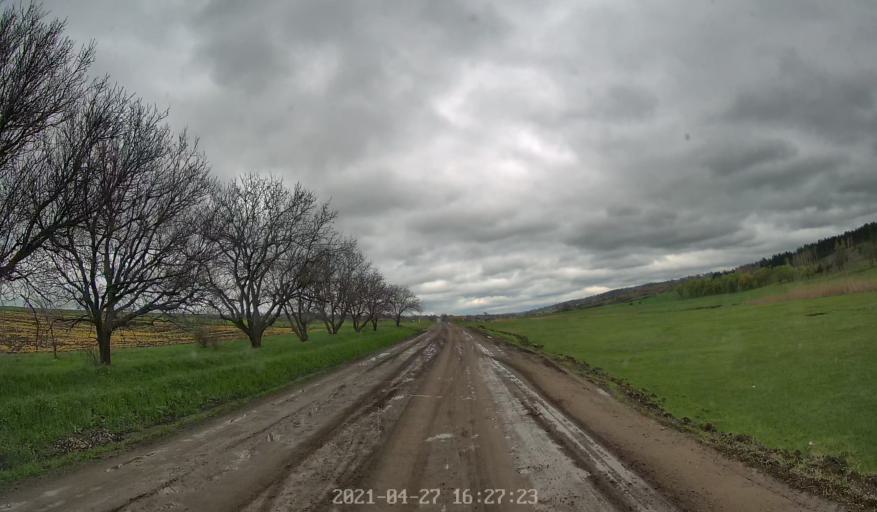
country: MD
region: Chisinau
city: Singera
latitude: 46.9757
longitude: 29.0336
